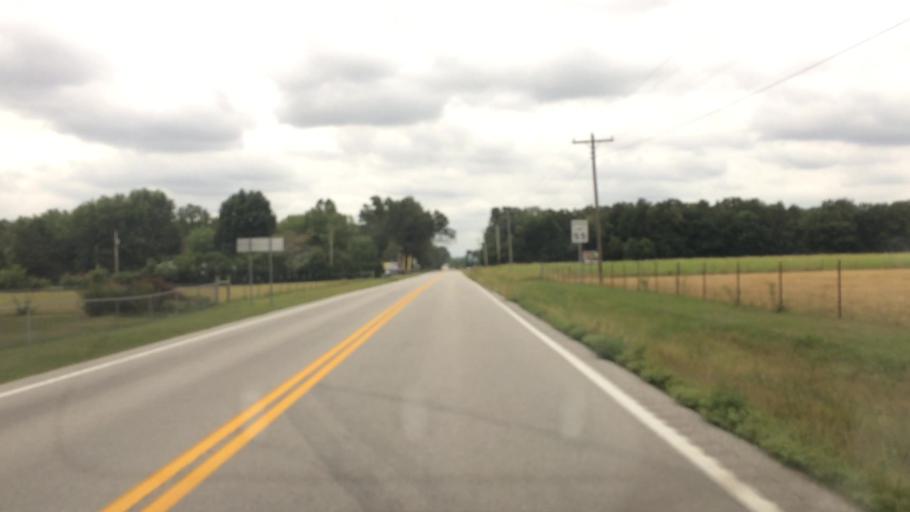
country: US
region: Missouri
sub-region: Greene County
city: Strafford
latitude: 37.2948
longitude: -93.1130
